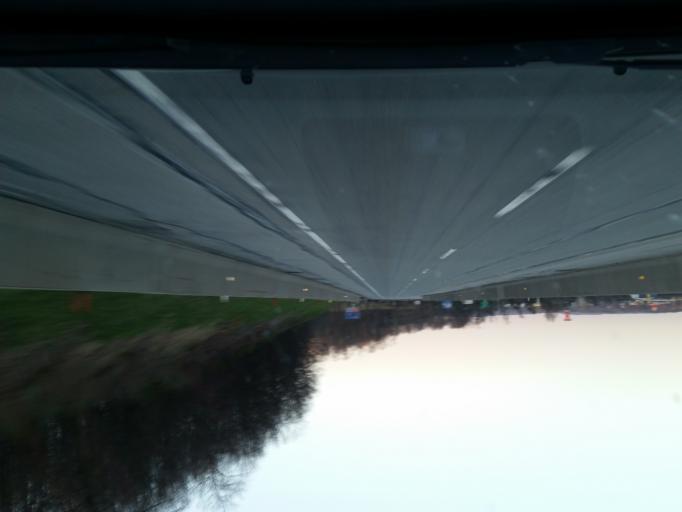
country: US
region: Pennsylvania
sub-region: Somerset County
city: Somerset
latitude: 40.0266
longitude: -79.0909
